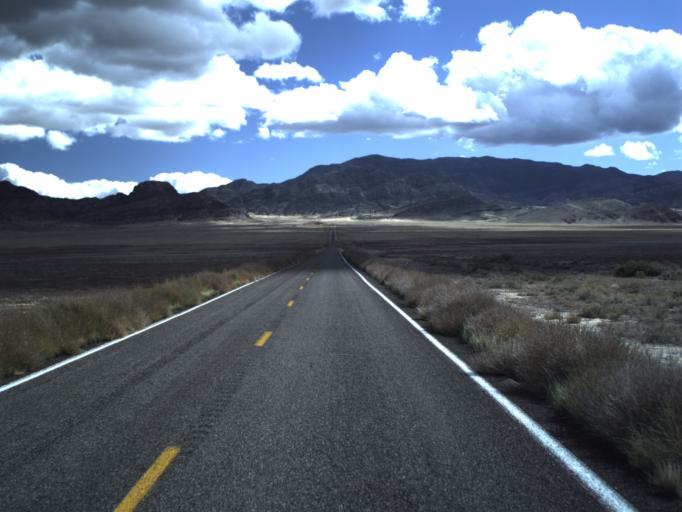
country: US
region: Utah
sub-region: Beaver County
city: Milford
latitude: 38.5238
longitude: -113.6588
